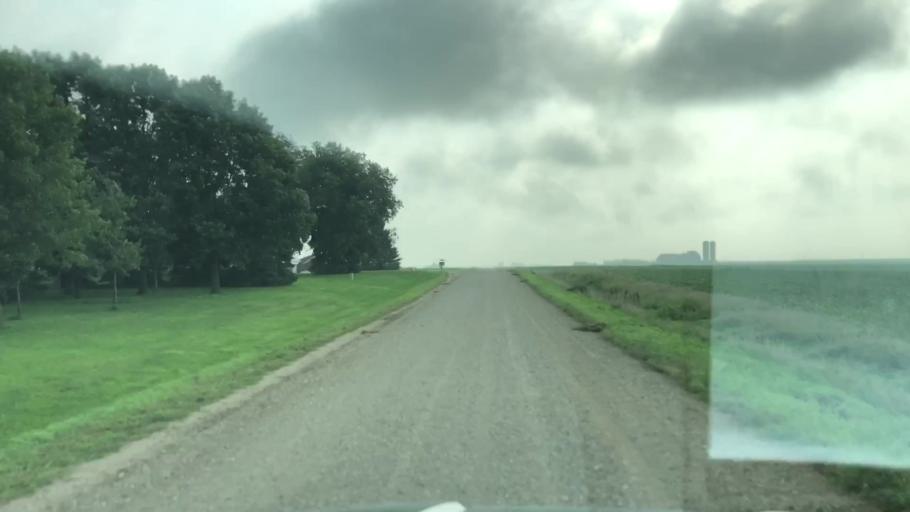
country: US
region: Iowa
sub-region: Sioux County
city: Hull
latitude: 43.2293
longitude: -96.0943
